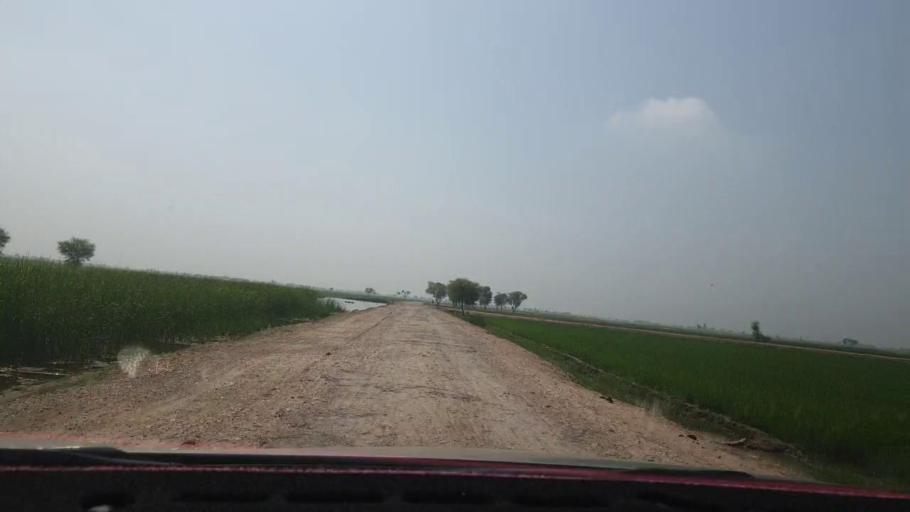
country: PK
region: Sindh
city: Nasirabad
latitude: 27.3998
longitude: 67.8492
